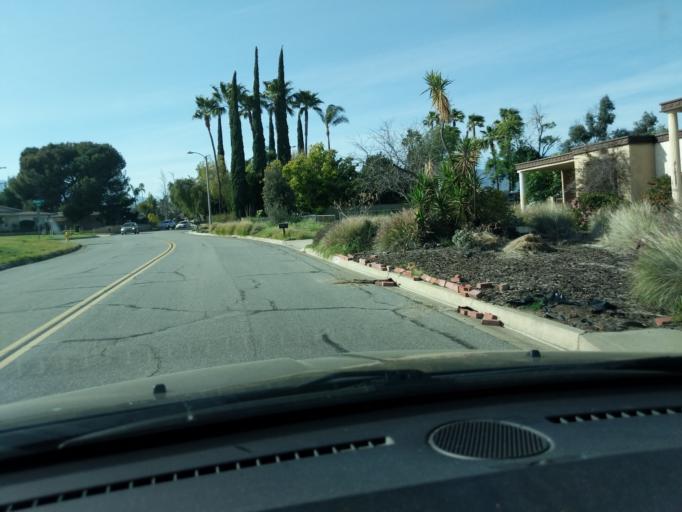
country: US
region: California
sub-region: San Bernardino County
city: Muscoy
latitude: 34.1451
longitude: -117.3739
